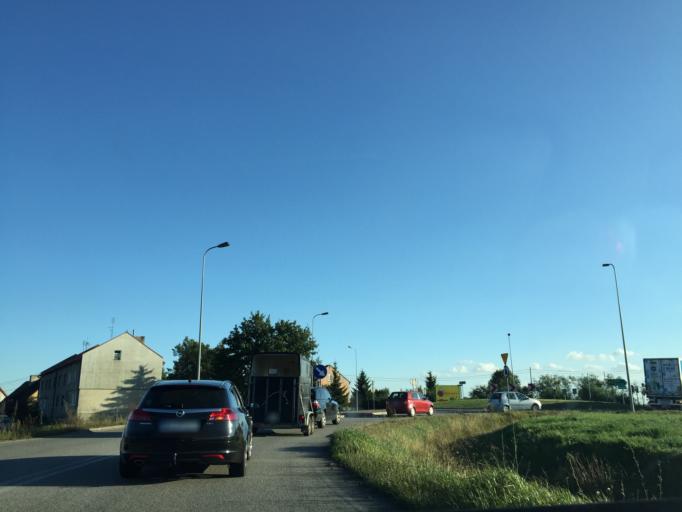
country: PL
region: Podlasie
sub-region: Powiat kolnenski
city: Stawiski
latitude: 53.3858
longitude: 22.1502
